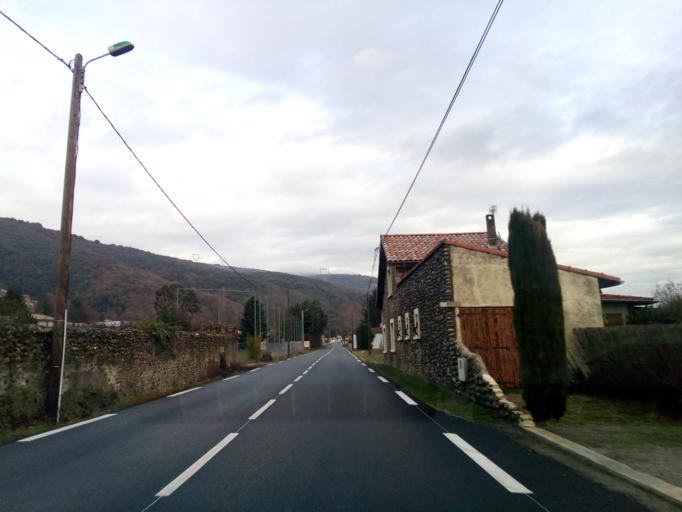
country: FR
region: Rhone-Alpes
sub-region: Departement de l'Ardeche
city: Saint-Laurent-du-Pape
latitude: 44.8259
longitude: 4.7741
